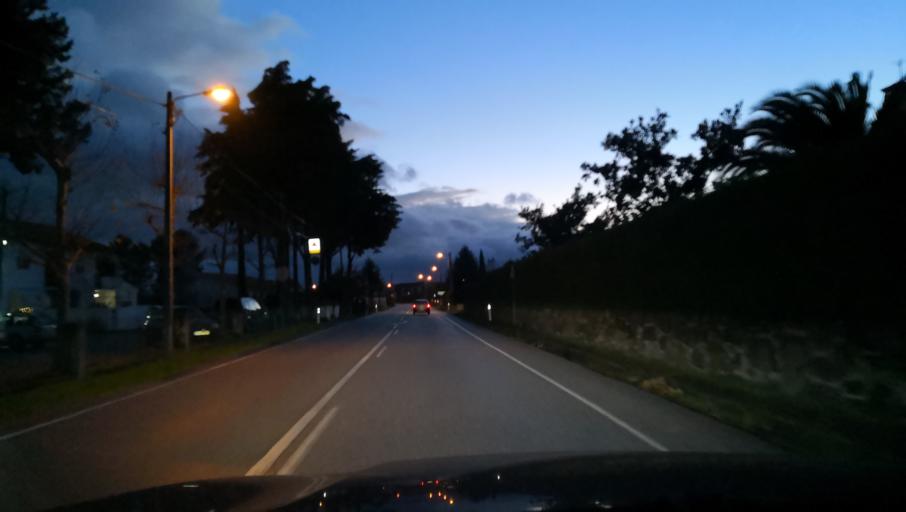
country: PT
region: Vila Real
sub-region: Vila Real
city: Vila Real
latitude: 41.3486
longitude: -7.7214
